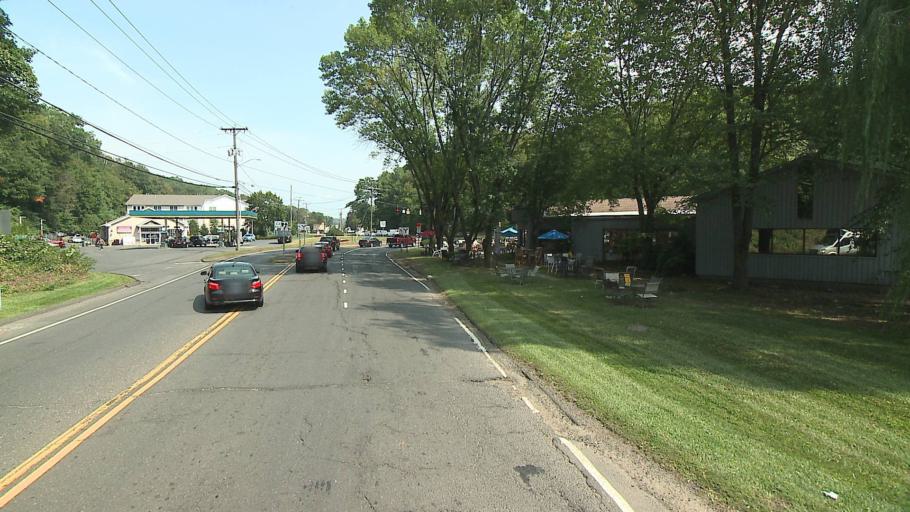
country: US
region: Connecticut
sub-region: Fairfield County
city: Ridgefield
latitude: 41.3210
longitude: -73.4767
